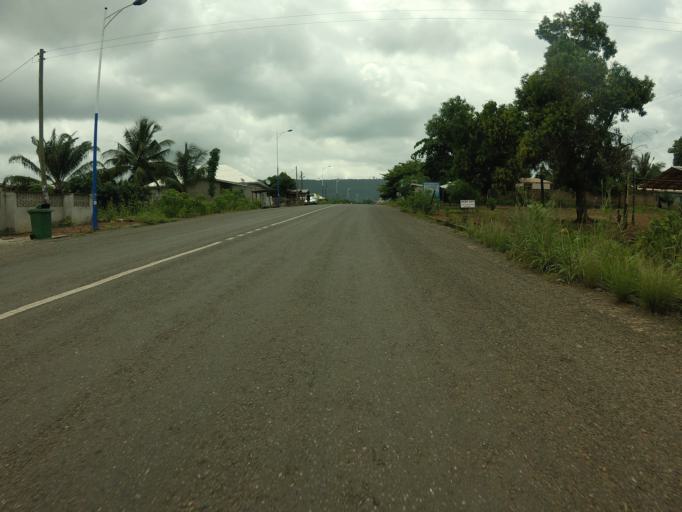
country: GH
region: Volta
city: Ho
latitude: 6.6248
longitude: 0.4906
